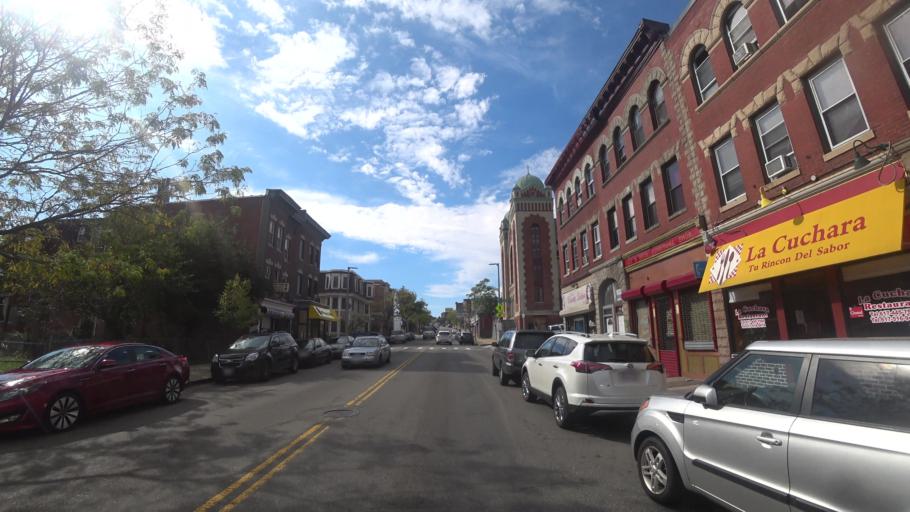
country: US
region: Massachusetts
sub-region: Suffolk County
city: South Boston
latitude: 42.3119
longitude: -71.0808
